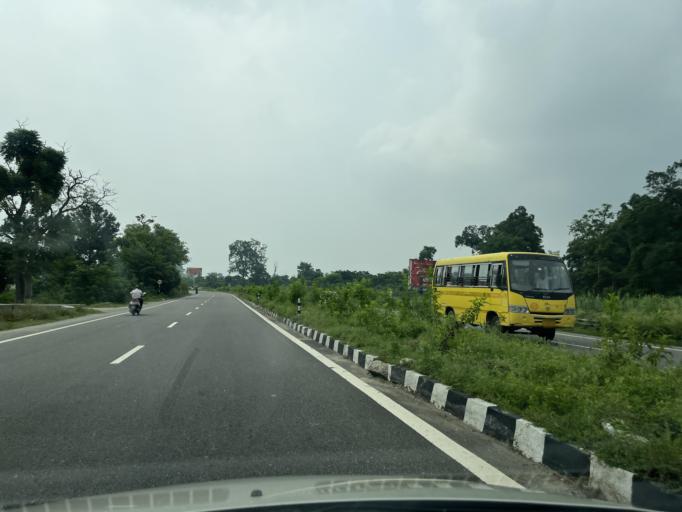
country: IN
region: Uttarakhand
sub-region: Dehradun
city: Raiwala
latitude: 30.0595
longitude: 78.2135
